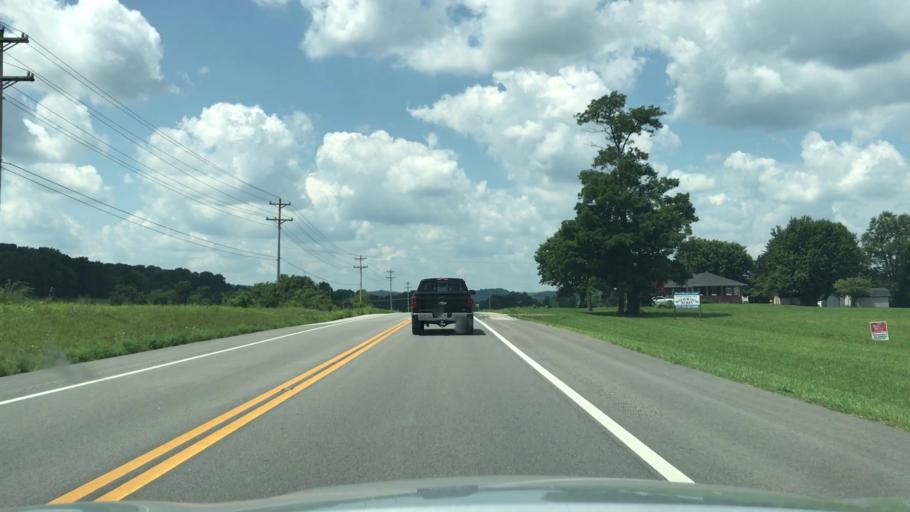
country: US
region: Tennessee
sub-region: Overton County
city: Livingston
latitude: 36.4442
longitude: -85.2244
